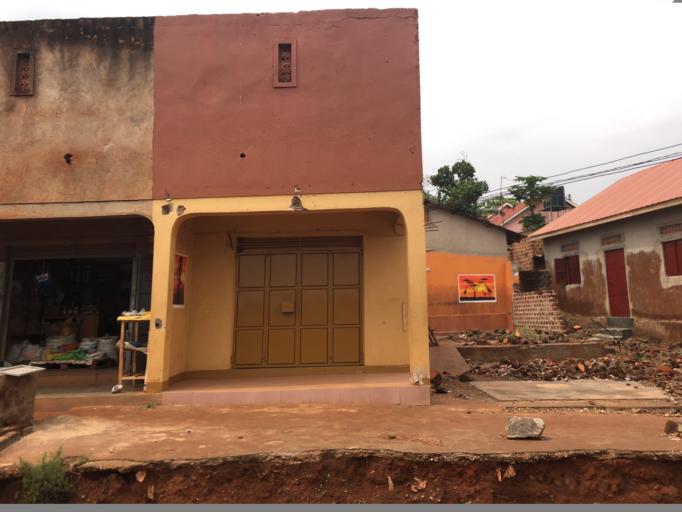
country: UG
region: Central Region
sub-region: Mukono District
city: Mukono
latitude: 0.3548
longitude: 32.7504
